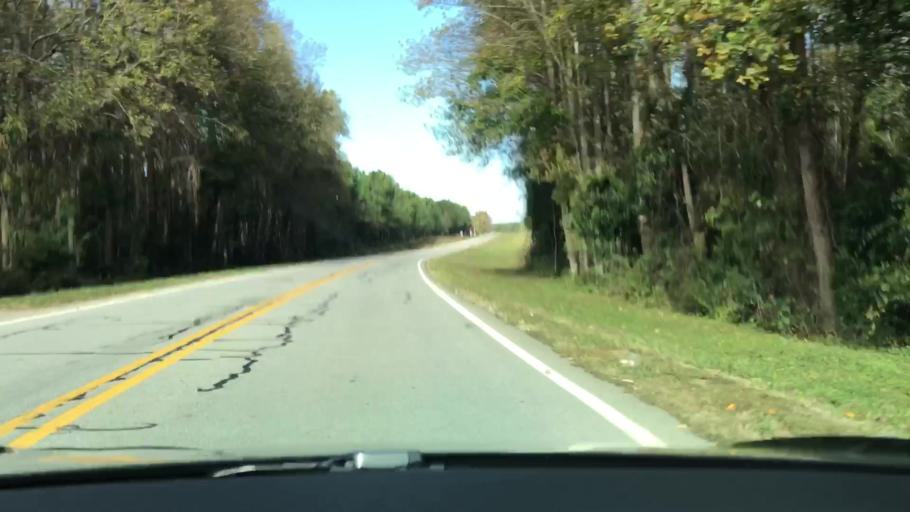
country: US
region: Georgia
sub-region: Glascock County
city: Gibson
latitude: 33.3343
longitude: -82.5678
